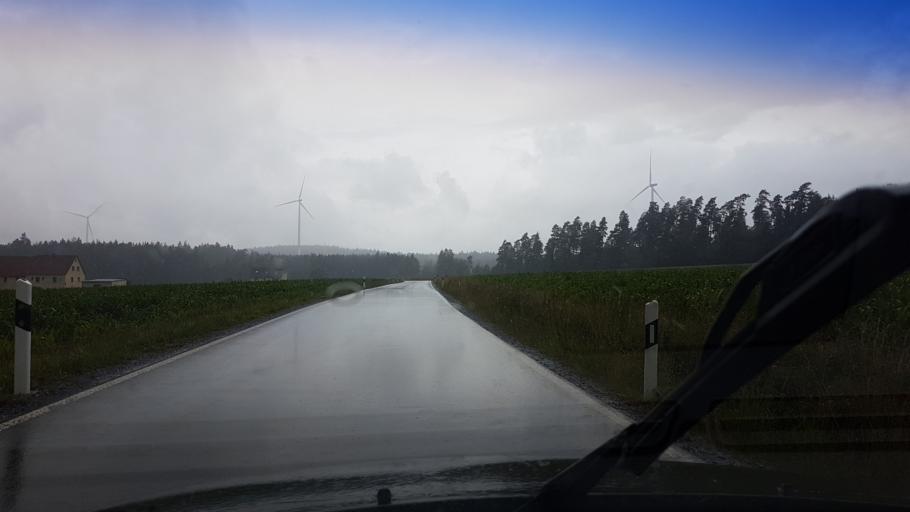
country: DE
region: Bavaria
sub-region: Upper Franconia
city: Schirnding
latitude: 50.0454
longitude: 12.2386
